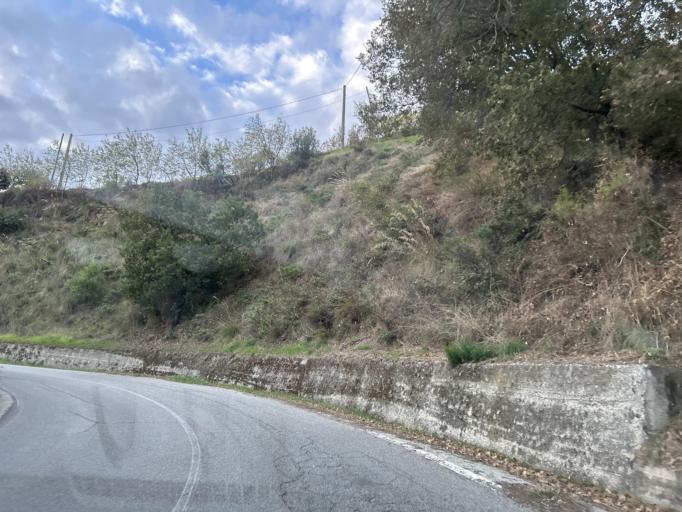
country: IT
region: Calabria
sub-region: Provincia di Catanzaro
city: Gasperina
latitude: 38.7447
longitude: 16.5071
